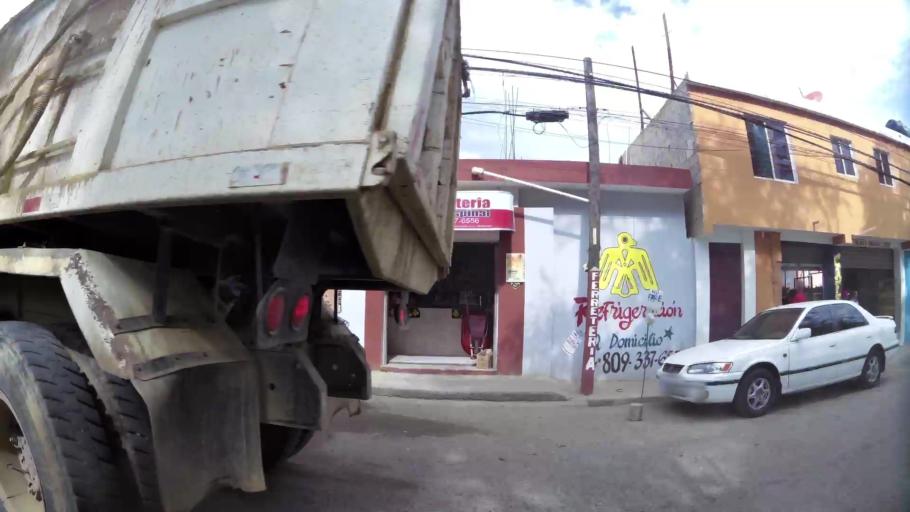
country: DO
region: Santiago
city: Santiago de los Caballeros
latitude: 19.4224
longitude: -70.7141
